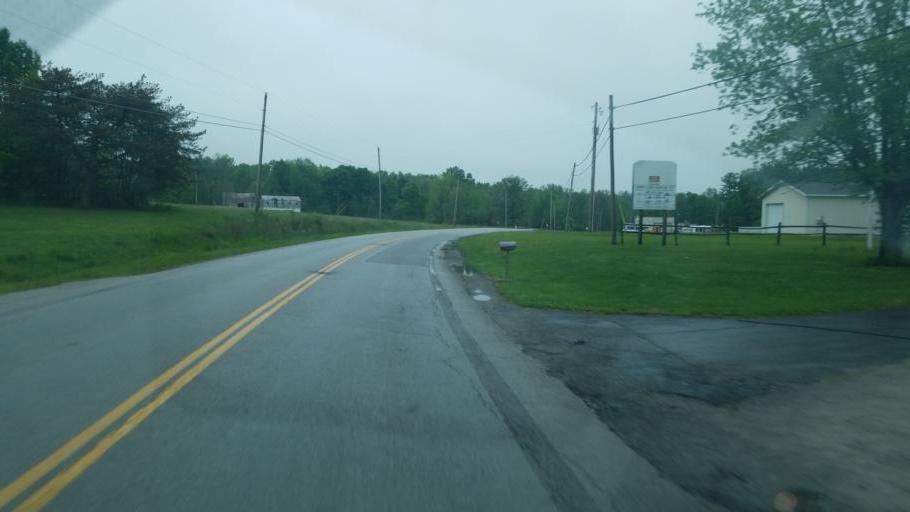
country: US
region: Ohio
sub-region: Highland County
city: Hillsboro
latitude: 39.2474
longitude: -83.6059
